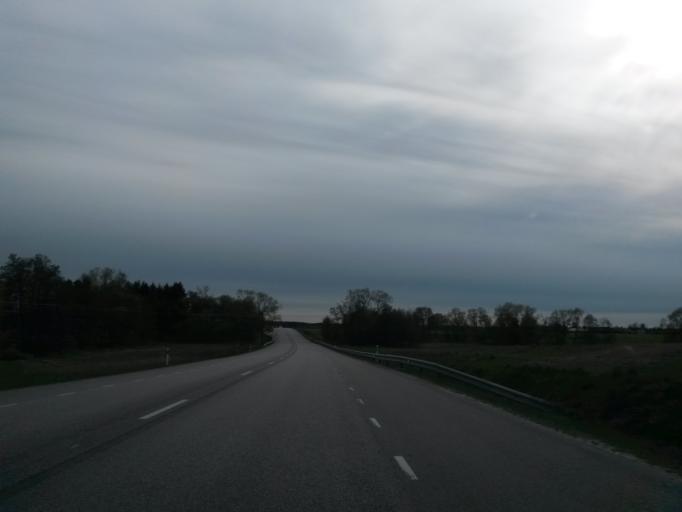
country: SE
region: Vaestra Goetaland
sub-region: Vara Kommun
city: Vara
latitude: 58.2455
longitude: 12.9471
